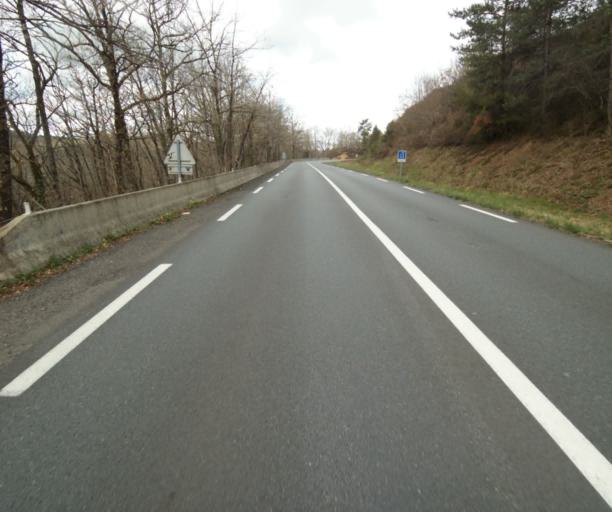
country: FR
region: Limousin
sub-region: Departement de la Correze
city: Sainte-Fortunade
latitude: 45.1883
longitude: 1.8439
